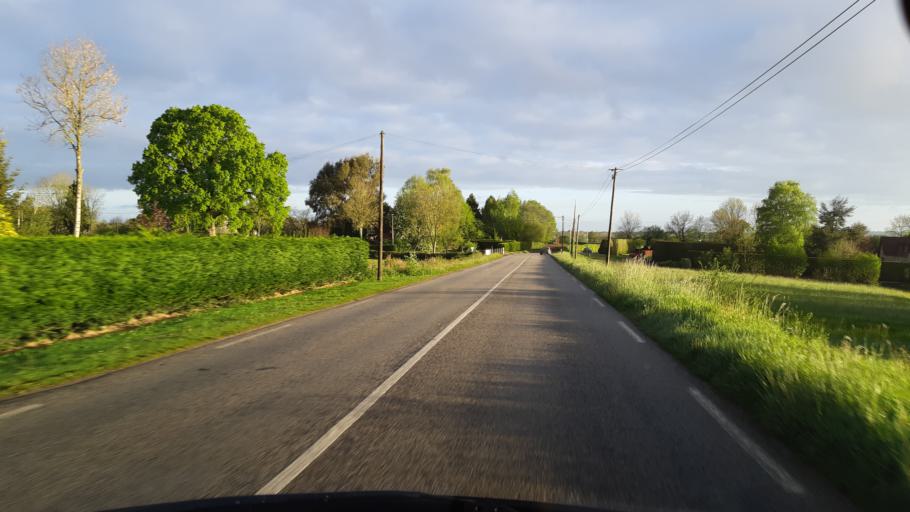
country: FR
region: Lower Normandy
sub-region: Departement de la Manche
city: Agneaux
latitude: 49.0573
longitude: -1.1329
